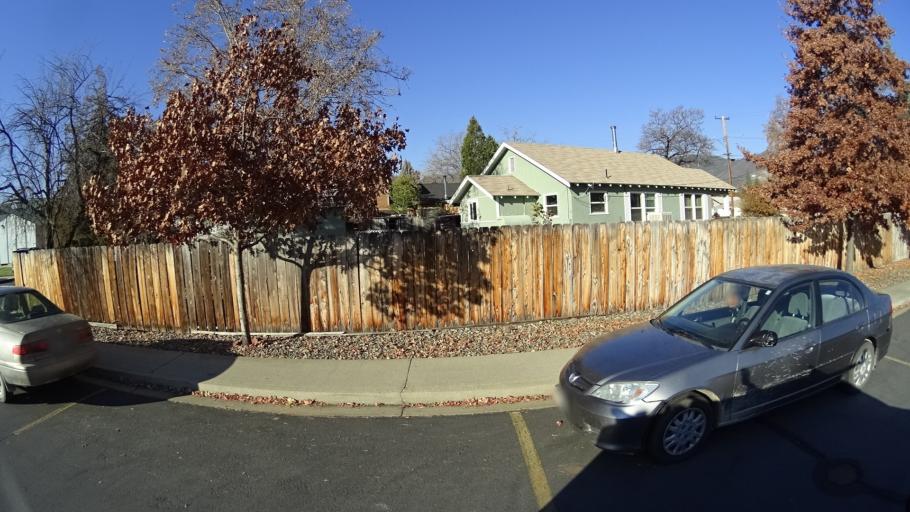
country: US
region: California
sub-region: Siskiyou County
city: Yreka
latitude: 41.7283
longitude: -122.6429
